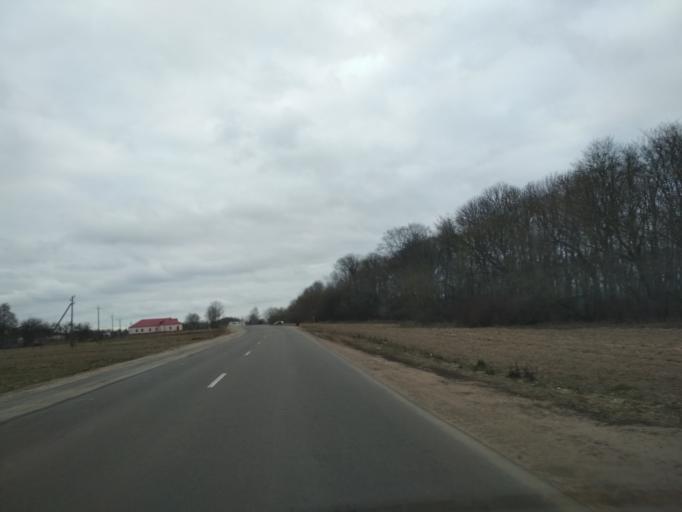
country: BY
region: Minsk
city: Druzhny
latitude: 53.5734
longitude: 27.9393
